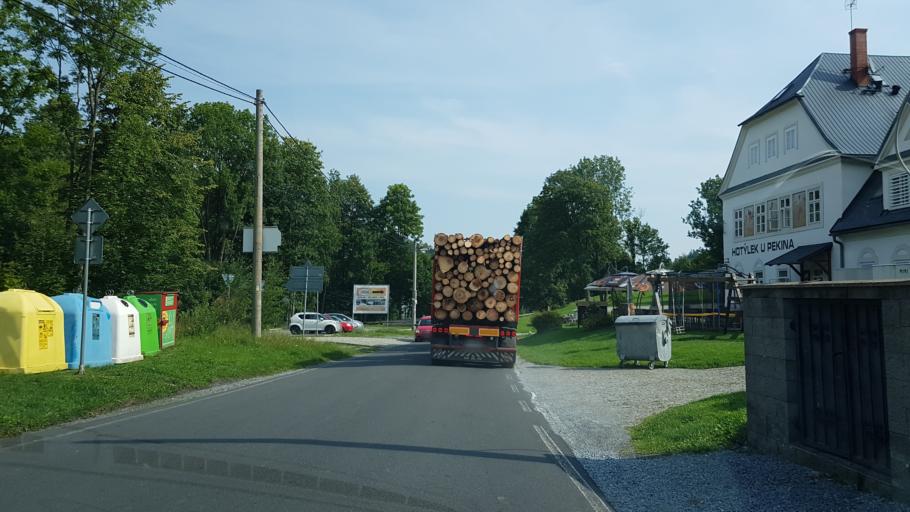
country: CZ
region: Olomoucky
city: Zlate Hory
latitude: 50.2400
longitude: 17.3462
